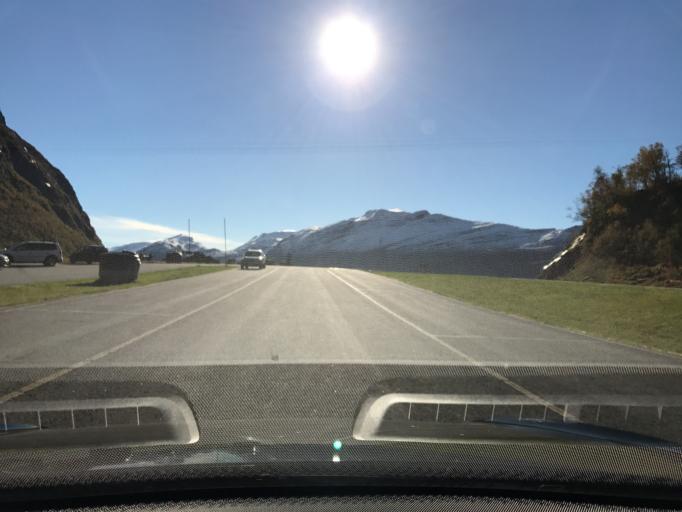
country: NO
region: More og Romsdal
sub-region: Norddal
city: Valldal
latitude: 62.1362
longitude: 7.1848
